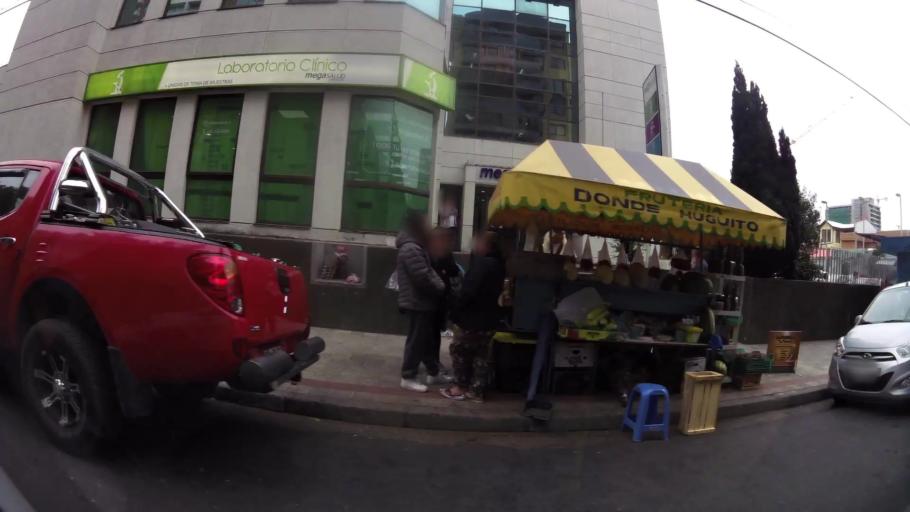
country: CL
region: Biobio
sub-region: Provincia de Concepcion
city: Concepcion
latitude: -36.8213
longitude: -73.0413
